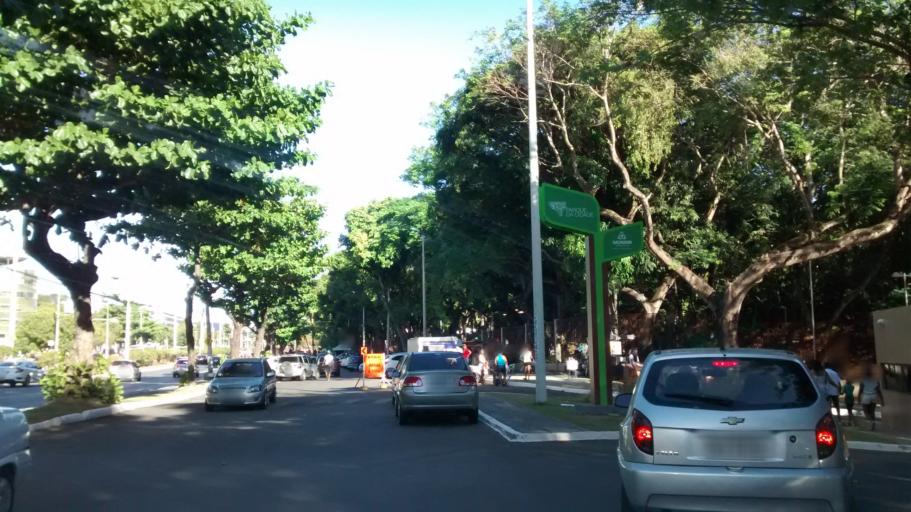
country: BR
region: Bahia
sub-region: Salvador
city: Salvador
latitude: -12.9962
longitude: -38.4727
